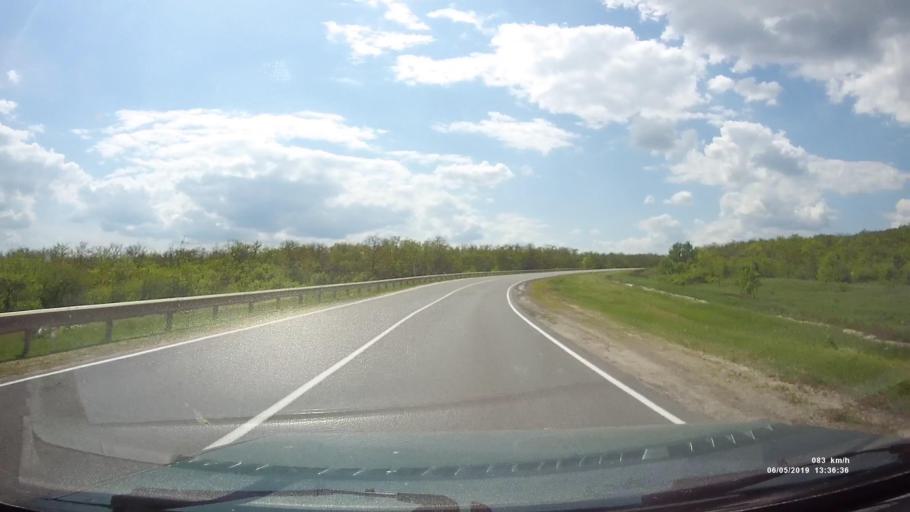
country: RU
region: Rostov
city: Ust'-Donetskiy
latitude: 47.6894
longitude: 40.7295
